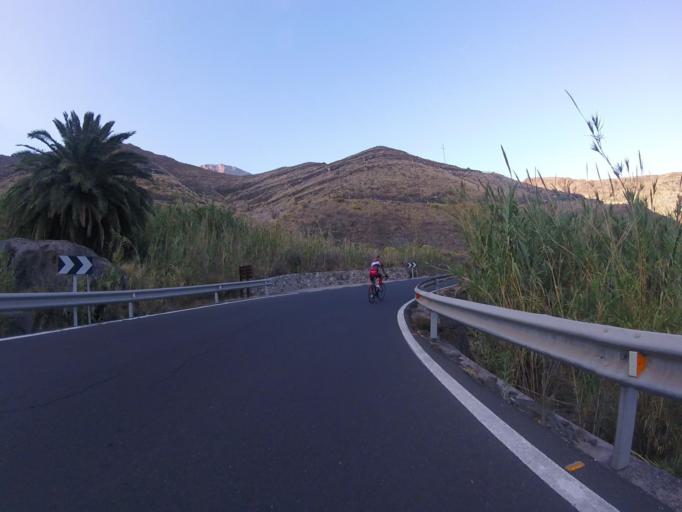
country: ES
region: Canary Islands
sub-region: Provincia de Las Palmas
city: Agaete
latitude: 28.0786
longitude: -15.7054
